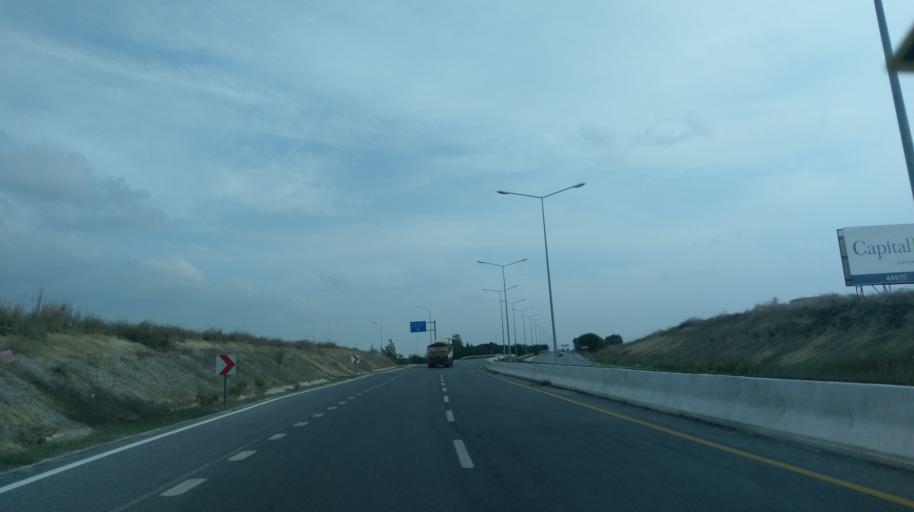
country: CY
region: Lefkosia
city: Mammari
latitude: 35.2186
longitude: 33.1772
